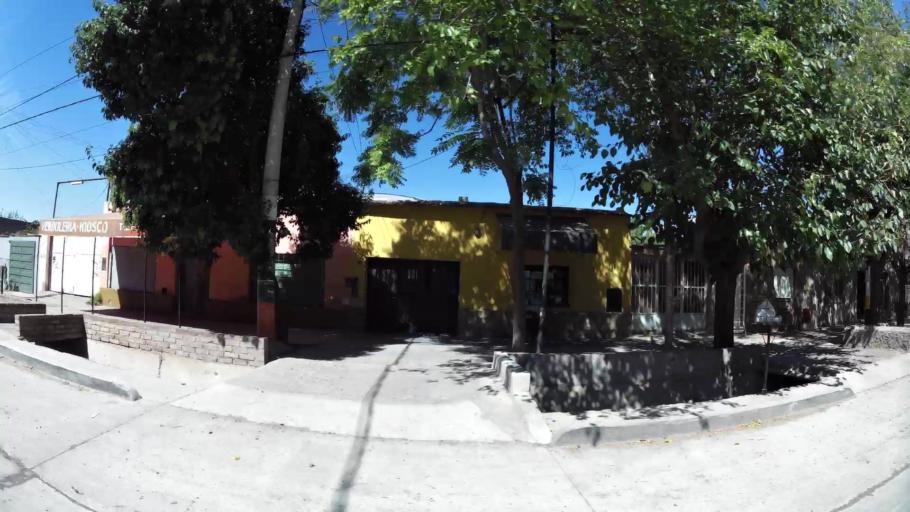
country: AR
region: Mendoza
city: Mendoza
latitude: -32.8938
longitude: -68.8135
